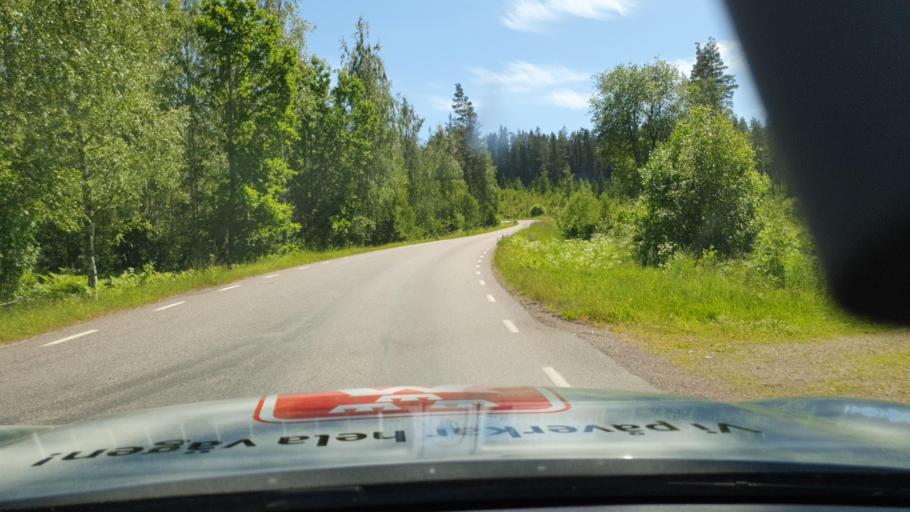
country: SE
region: Vaestra Goetaland
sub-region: Tidaholms Kommun
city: Tidaholm
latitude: 58.0842
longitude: 13.9458
